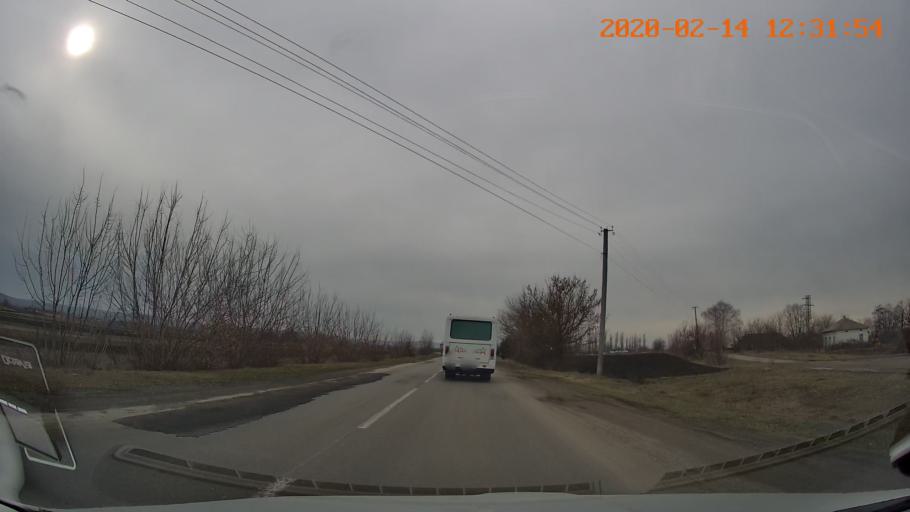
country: RO
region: Botosani
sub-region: Comuna Darabani
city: Bajura
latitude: 48.2466
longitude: 26.5535
